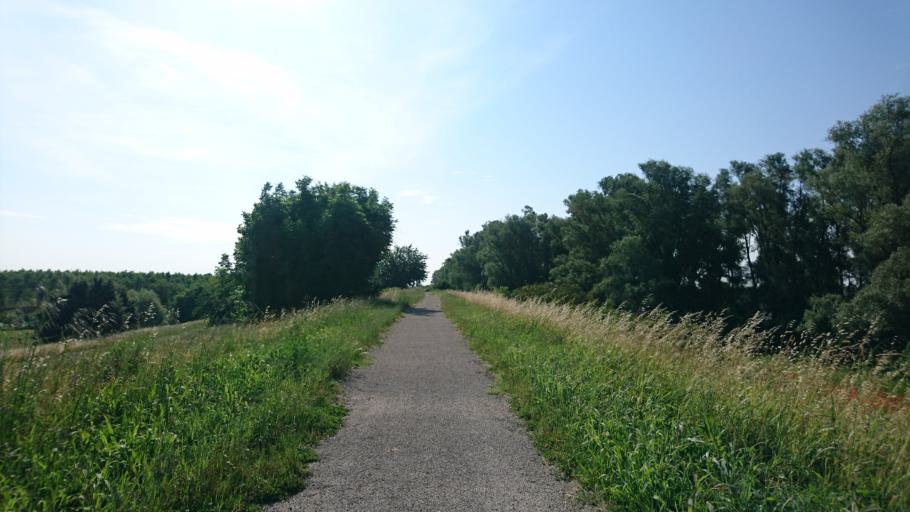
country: IT
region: Veneto
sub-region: Provincia di Verona
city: Villa Bartolomea
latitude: 45.1734
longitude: 11.3398
